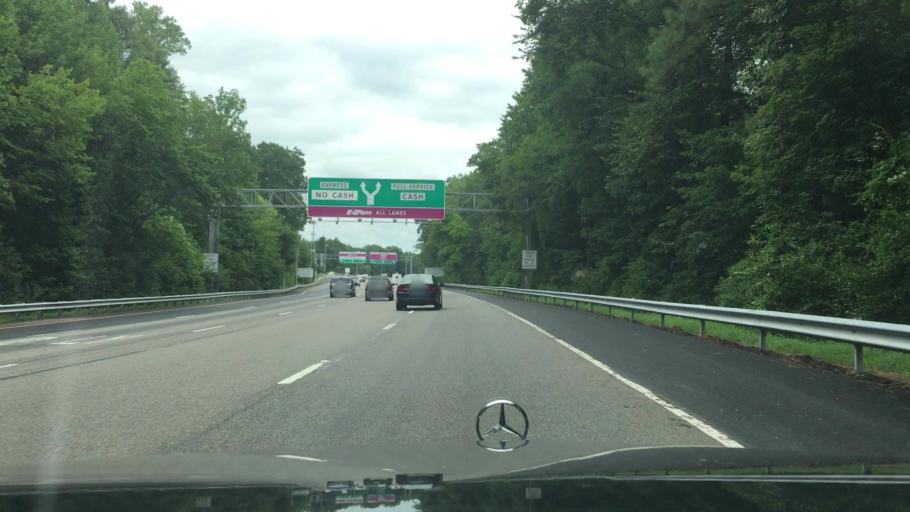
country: US
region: Virginia
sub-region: Chesterfield County
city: Bon Air
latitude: 37.5292
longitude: -77.5212
